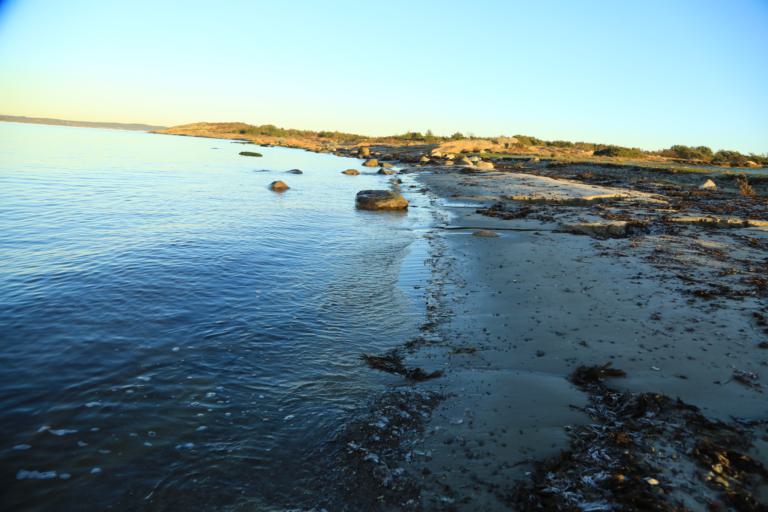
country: SE
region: Halland
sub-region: Kungsbacka Kommun
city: Frillesas
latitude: 57.1966
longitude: 12.1599
